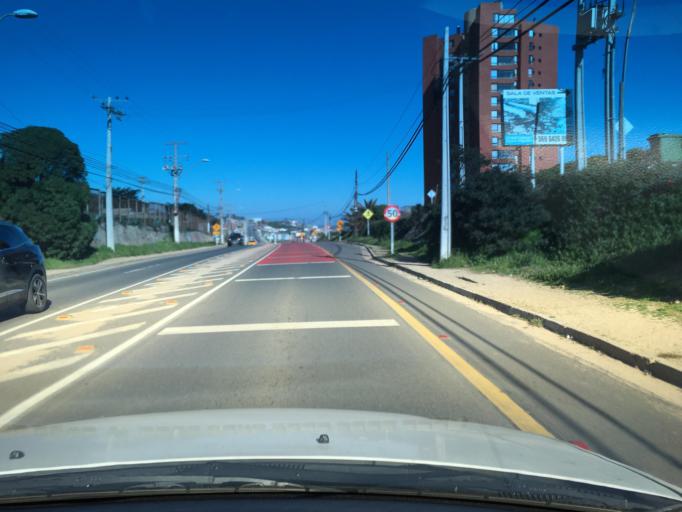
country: CL
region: Valparaiso
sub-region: San Antonio Province
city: El Tabo
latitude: -33.4482
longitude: -71.6769
